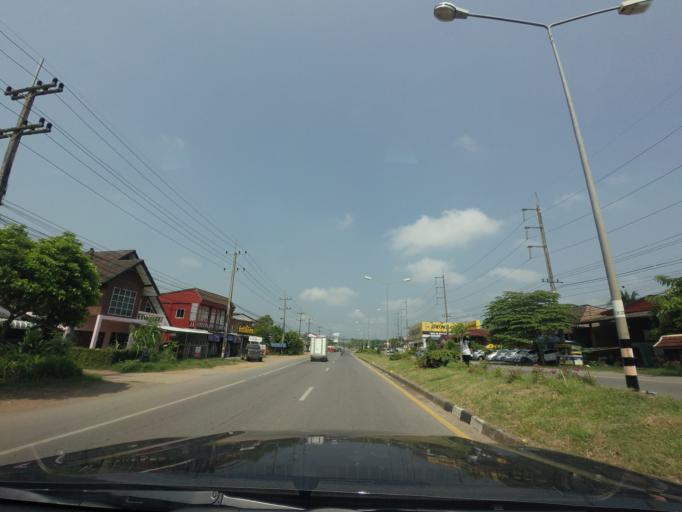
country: TH
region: Nan
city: Nan
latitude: 18.7839
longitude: 100.7462
